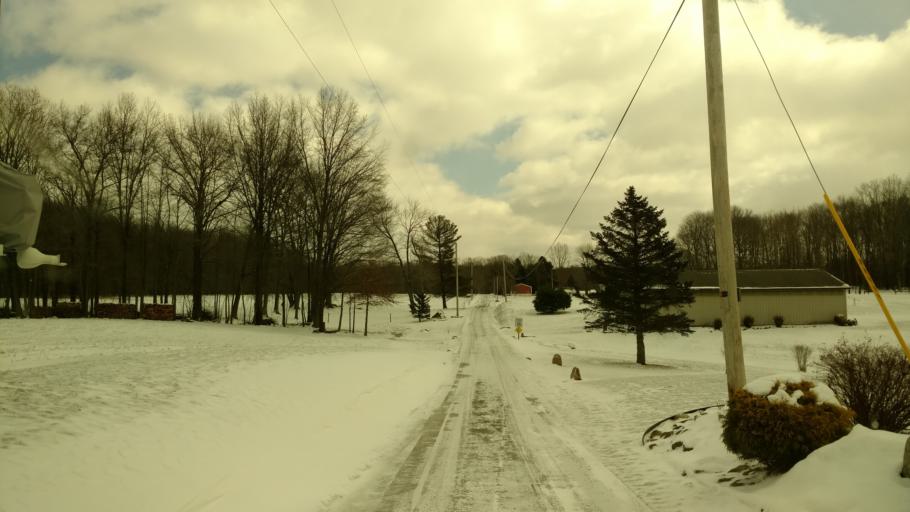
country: US
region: Pennsylvania
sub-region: Mercer County
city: Mercer
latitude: 41.3423
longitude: -80.2262
